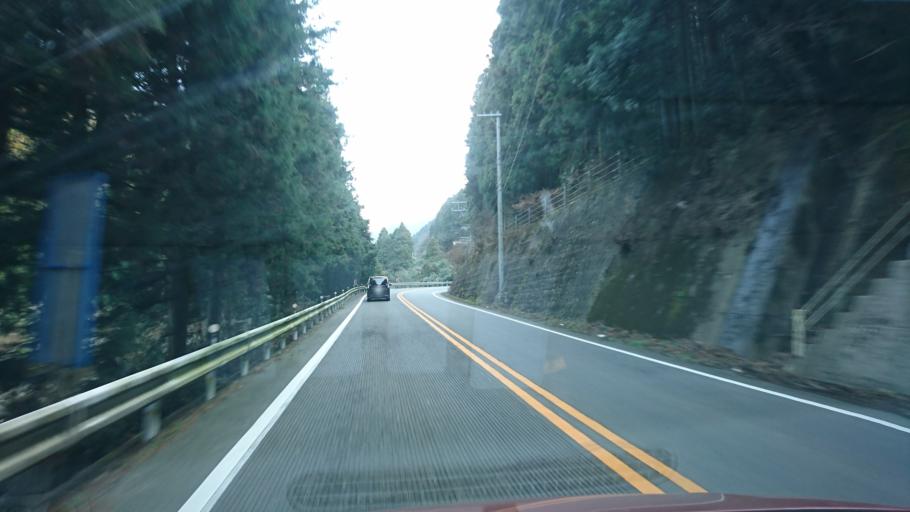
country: JP
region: Ehime
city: Hojo
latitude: 33.9659
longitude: 132.9055
